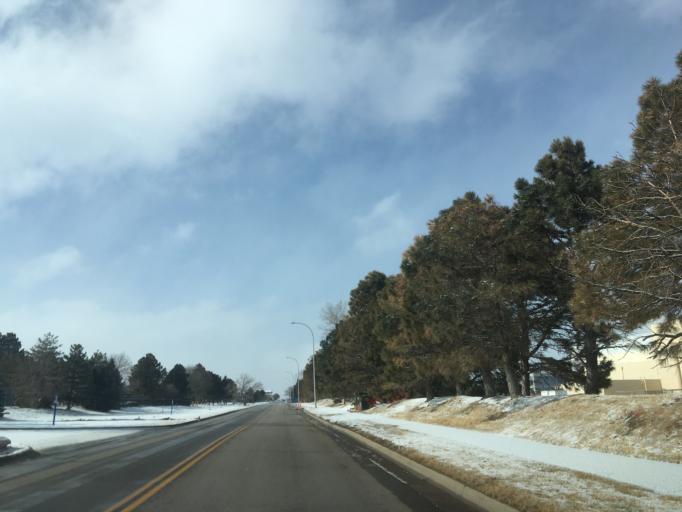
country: US
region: Colorado
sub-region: Broomfield County
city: Broomfield
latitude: 39.9098
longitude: -105.1026
